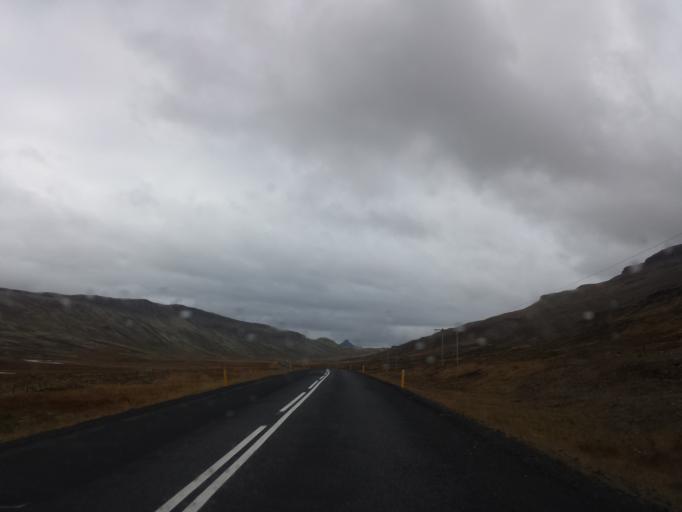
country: IS
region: West
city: Stykkisholmur
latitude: 64.8828
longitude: -22.8053
